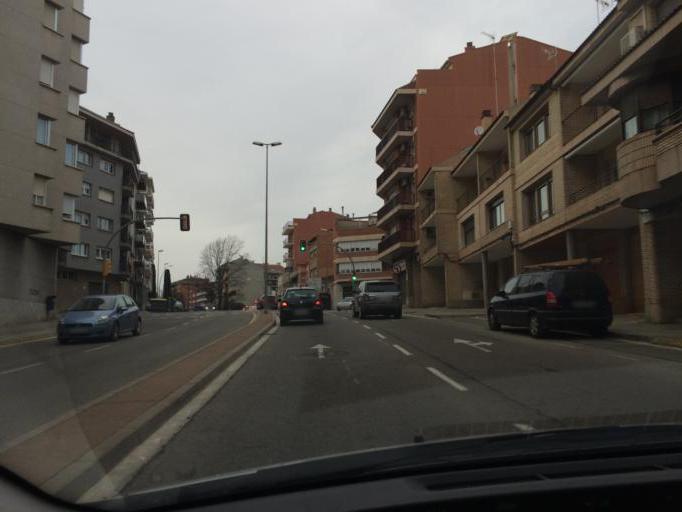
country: ES
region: Catalonia
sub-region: Provincia de Barcelona
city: Manresa
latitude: 41.7357
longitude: 1.8341
